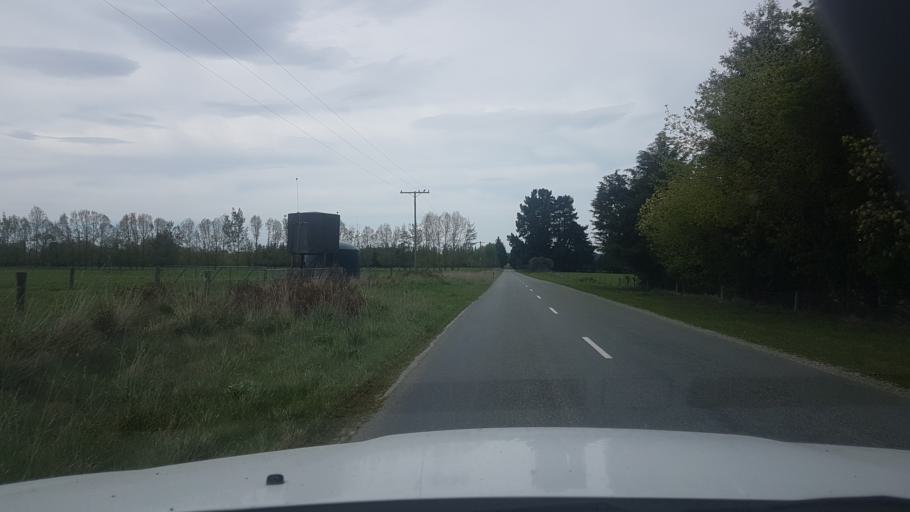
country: NZ
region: Canterbury
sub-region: Timaru District
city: Pleasant Point
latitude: -44.0718
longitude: 171.1525
